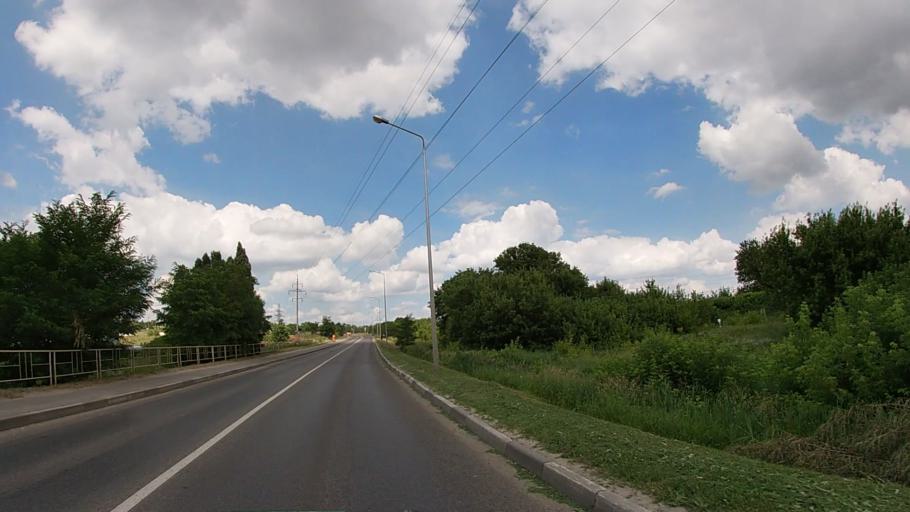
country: RU
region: Belgorod
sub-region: Belgorodskiy Rayon
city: Belgorod
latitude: 50.5923
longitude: 36.5619
